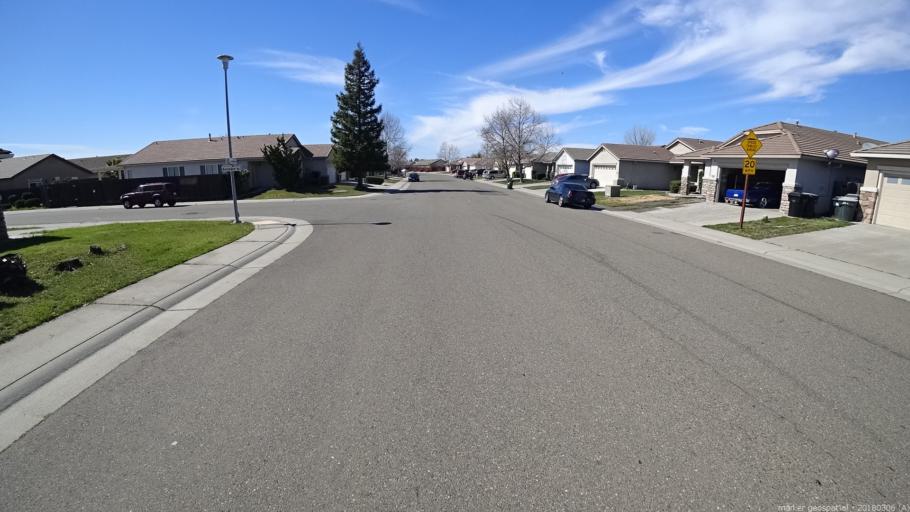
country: US
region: California
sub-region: Sacramento County
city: Vineyard
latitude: 38.4740
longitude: -121.3538
